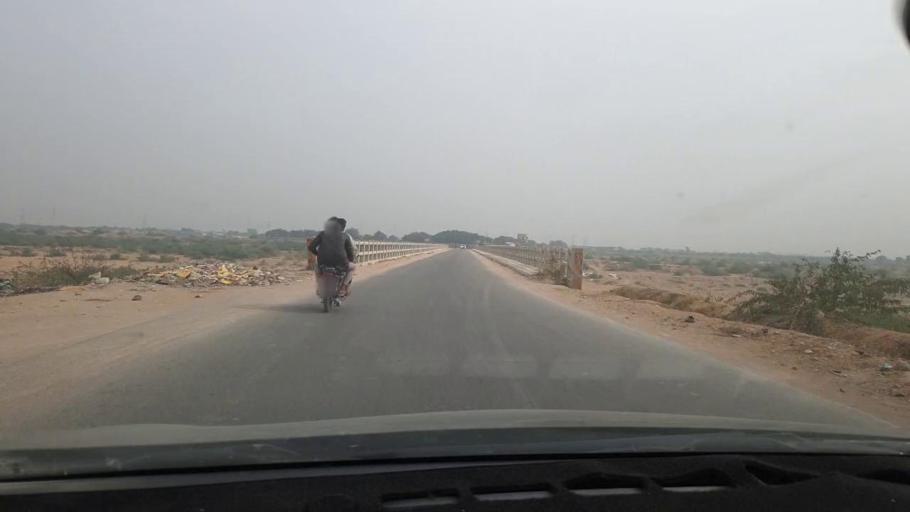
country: PK
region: Sindh
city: Malir Cantonment
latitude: 24.9145
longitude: 67.2656
